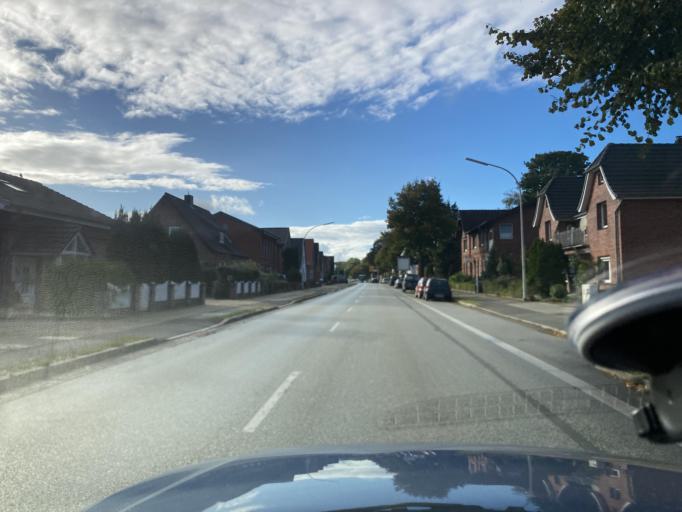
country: DE
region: Schleswig-Holstein
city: Rendsburg
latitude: 54.3093
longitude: 9.6363
